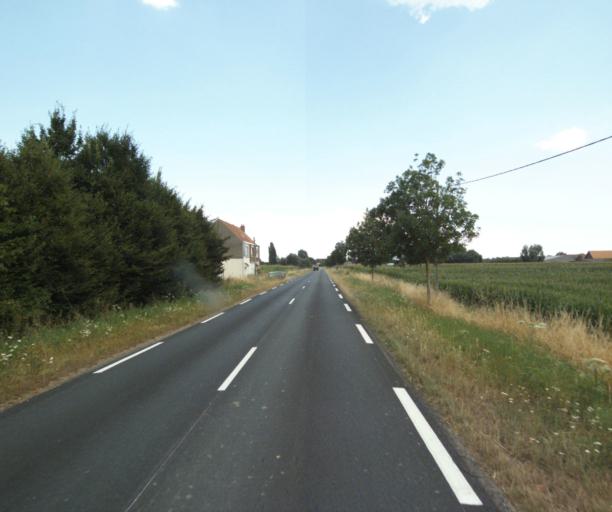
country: FR
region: Nord-Pas-de-Calais
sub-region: Departement du Nord
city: Deulemont
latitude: 50.7170
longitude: 2.9713
